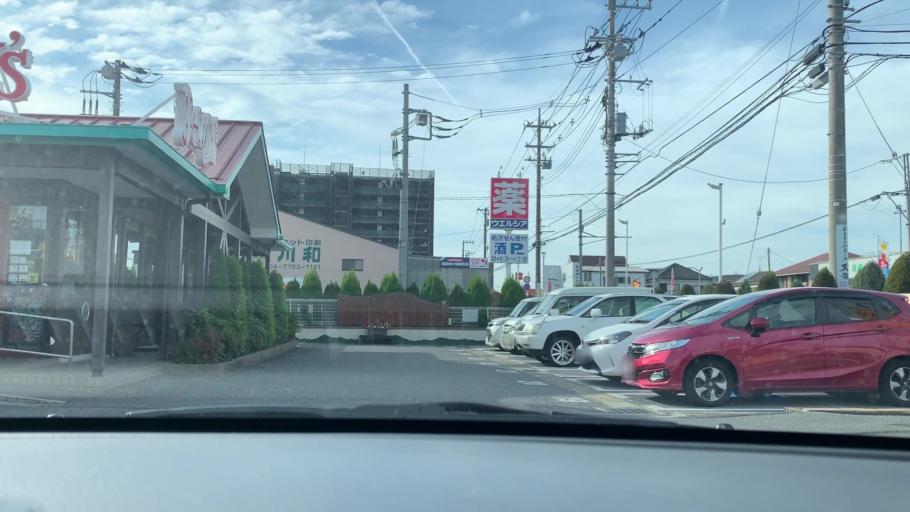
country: JP
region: Chiba
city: Nagareyama
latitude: 35.8847
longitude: 139.9159
